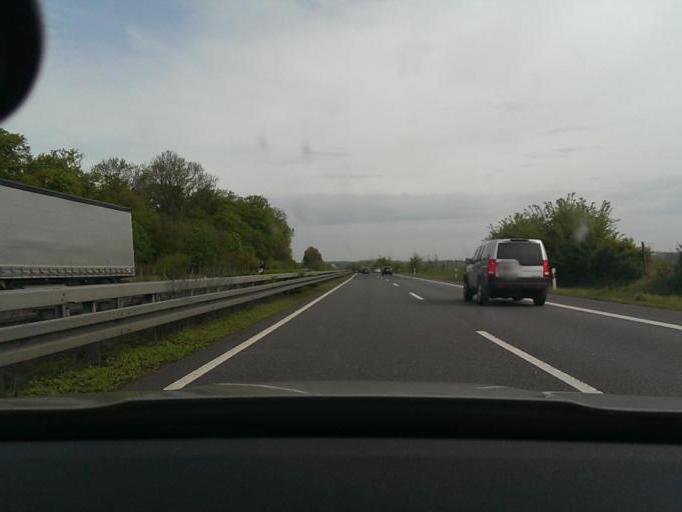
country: DE
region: Lower Saxony
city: Lehre
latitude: 52.3416
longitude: 10.7322
